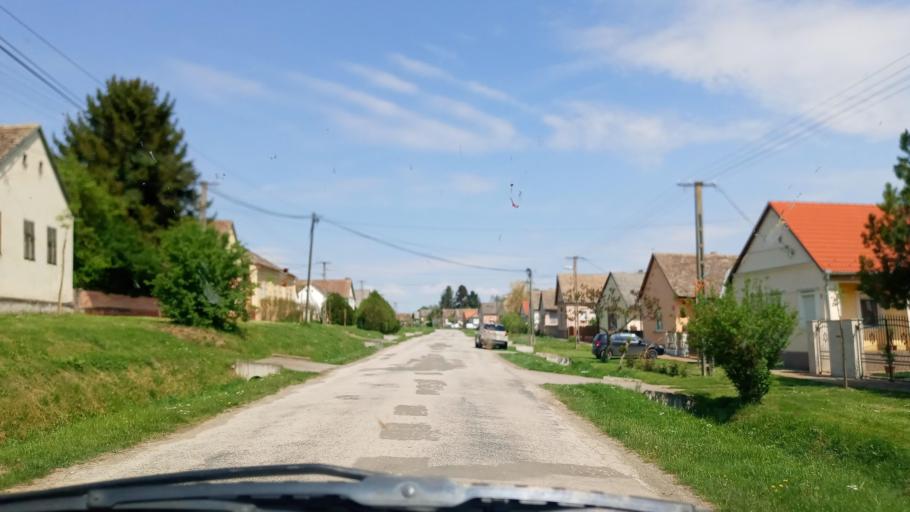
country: HR
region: Osjecko-Baranjska
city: Beli Manastir
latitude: 45.8653
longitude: 18.5857
